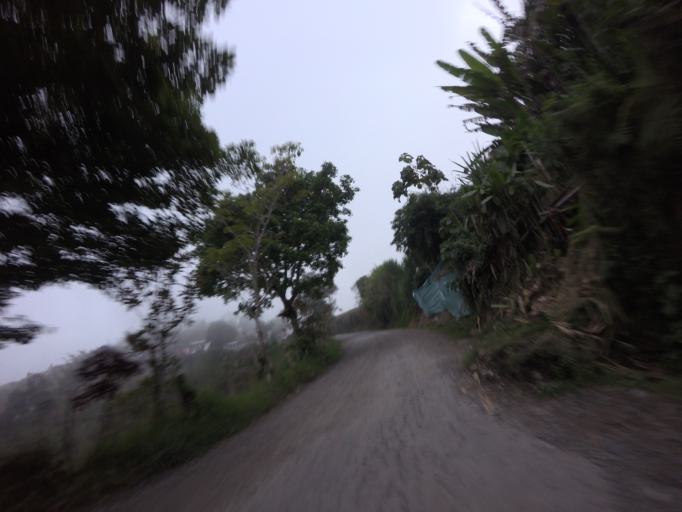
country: CO
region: Caldas
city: Manzanares
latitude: 5.3216
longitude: -75.1194
